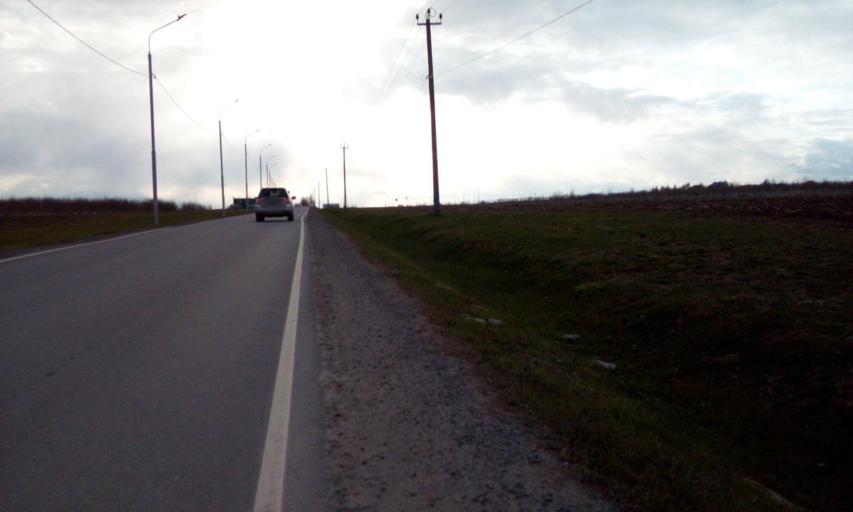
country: RU
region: Moskovskaya
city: Annino
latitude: 55.5231
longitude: 37.2472
